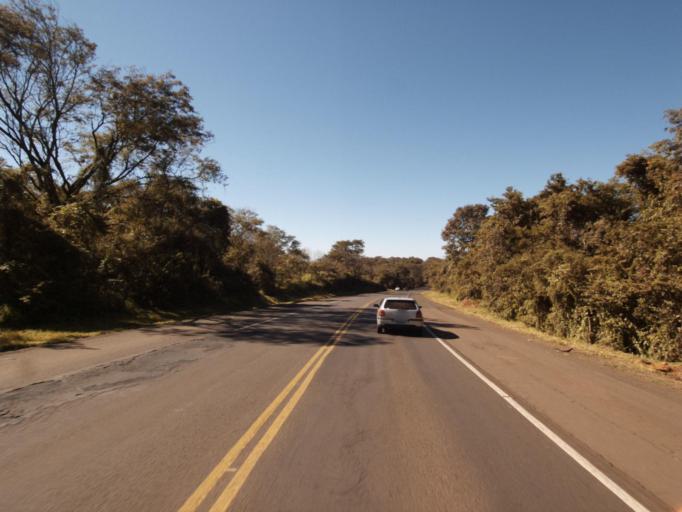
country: BR
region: Santa Catarina
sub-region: Chapeco
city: Chapeco
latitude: -26.9000
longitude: -52.8876
